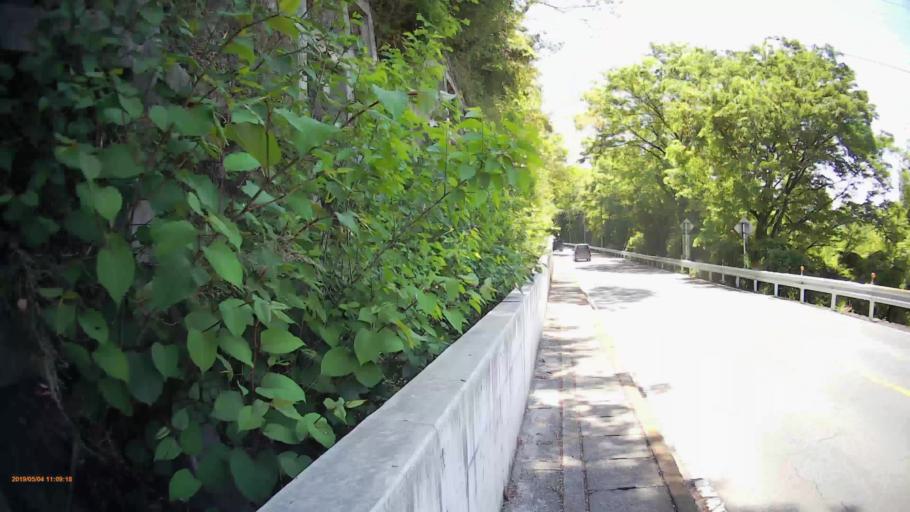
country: JP
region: Yamanashi
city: Nirasaki
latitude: 35.6973
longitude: 138.4692
